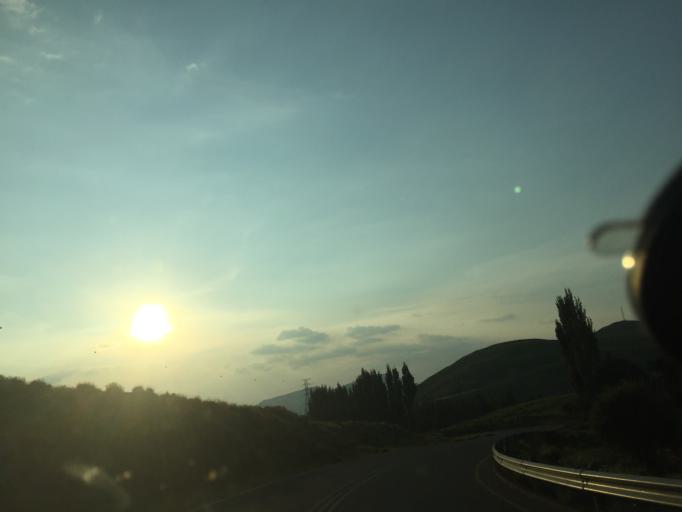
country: LS
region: Maseru
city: Nako
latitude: -29.4201
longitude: 27.9264
